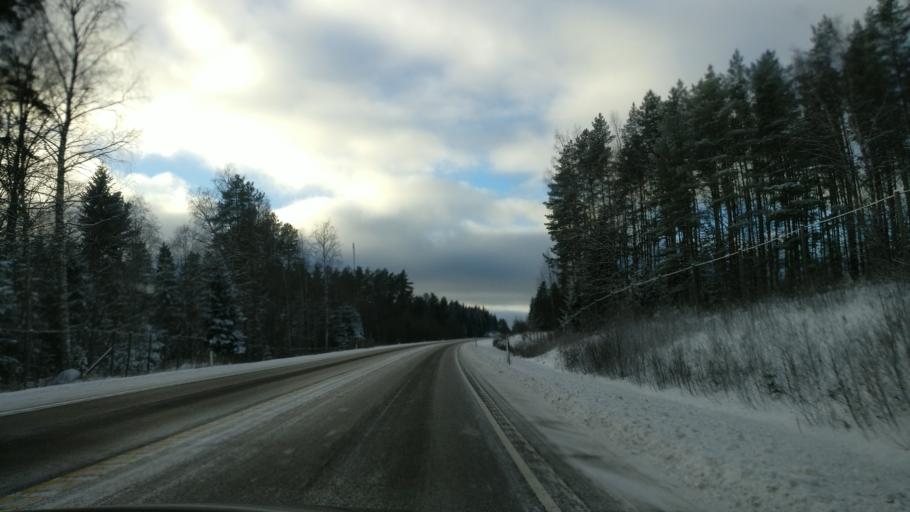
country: FI
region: Southern Savonia
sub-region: Mikkeli
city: Pertunmaa
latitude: 61.3682
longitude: 26.2784
